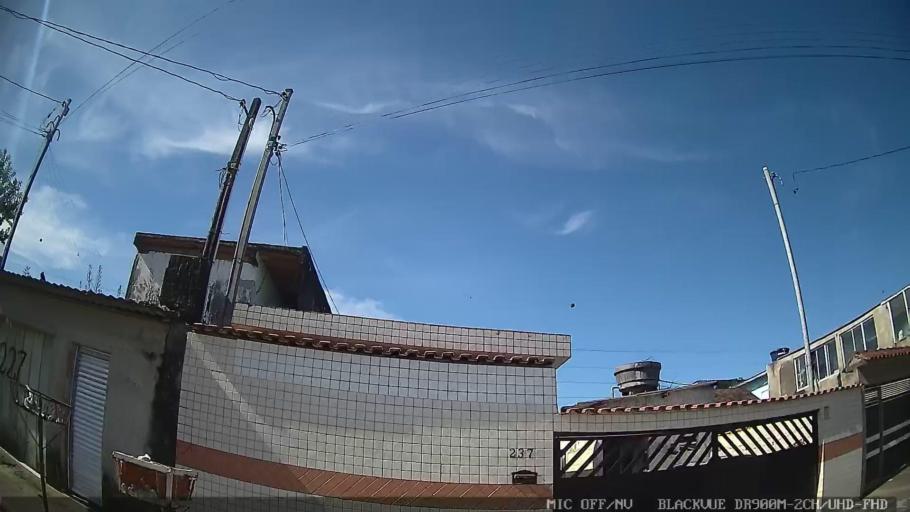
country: BR
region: Sao Paulo
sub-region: Santos
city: Santos
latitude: -23.9450
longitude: -46.2841
